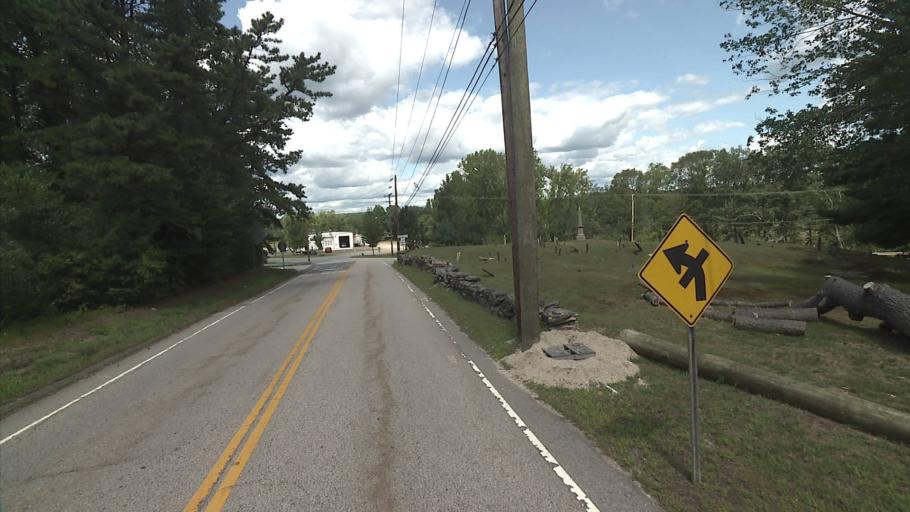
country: US
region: Connecticut
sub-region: New London County
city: Lisbon
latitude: 41.6146
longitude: -72.0363
